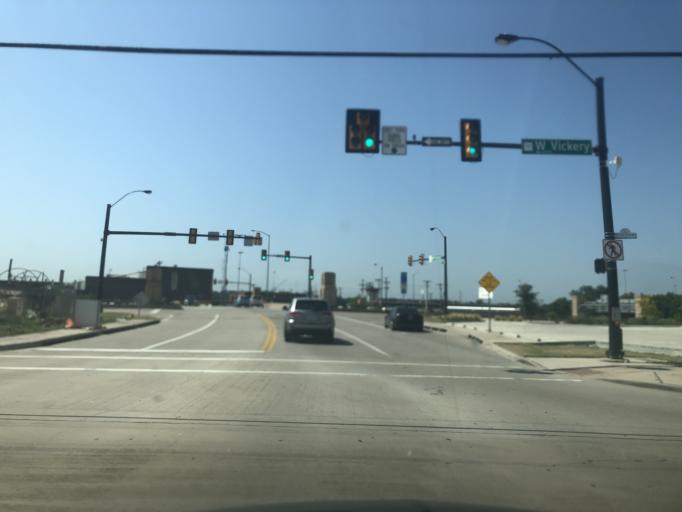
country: US
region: Texas
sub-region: Tarrant County
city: Westworth
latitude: 32.7301
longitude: -97.3701
